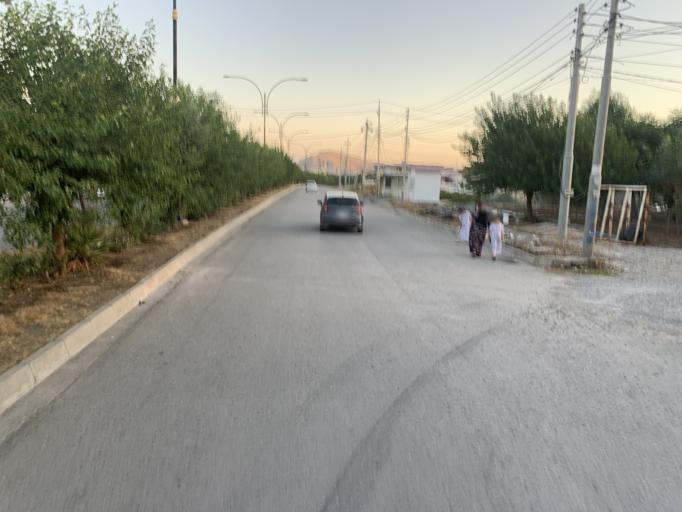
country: IQ
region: As Sulaymaniyah
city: Raniye
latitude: 36.2442
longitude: 44.8772
